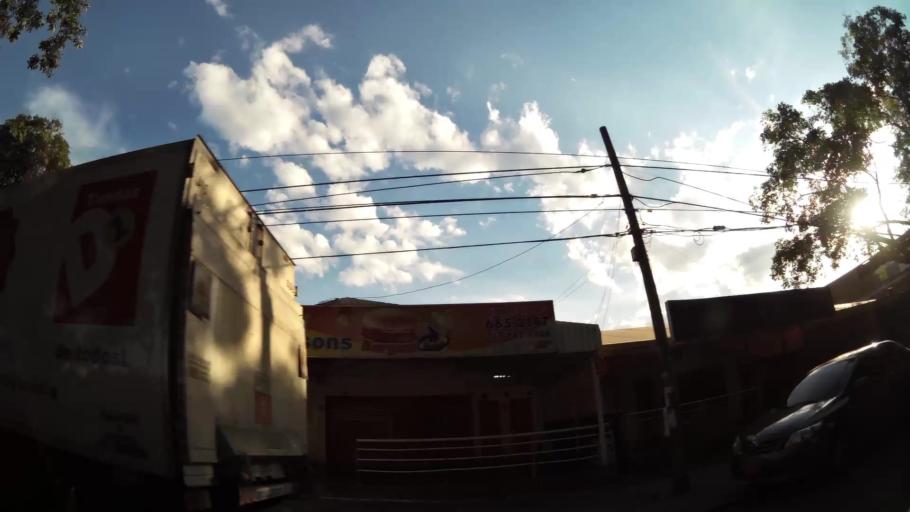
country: CO
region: Valle del Cauca
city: Cali
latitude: 3.4798
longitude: -76.5202
